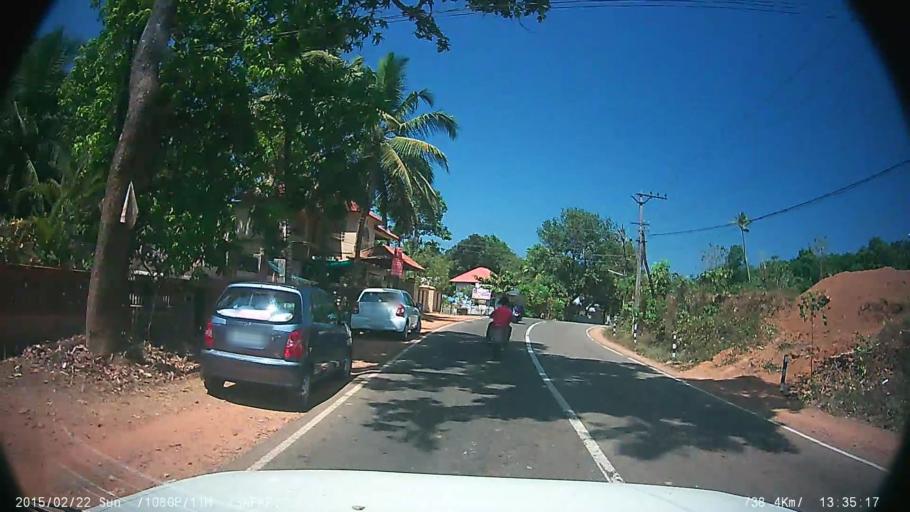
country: IN
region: Kerala
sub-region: Kottayam
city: Changanacheri
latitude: 9.4823
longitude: 76.6066
